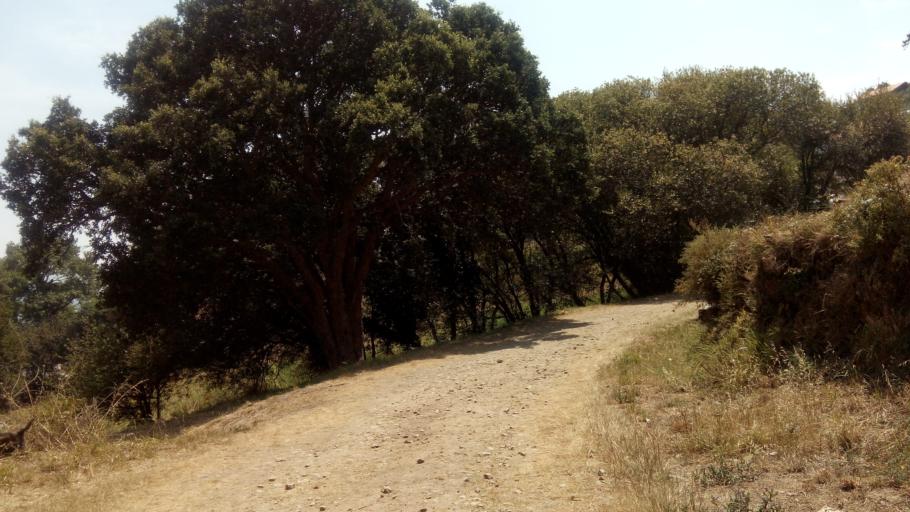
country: ES
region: Galicia
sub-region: Provincia de Pontevedra
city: Sanxenxo
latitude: 42.3782
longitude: -8.9328
